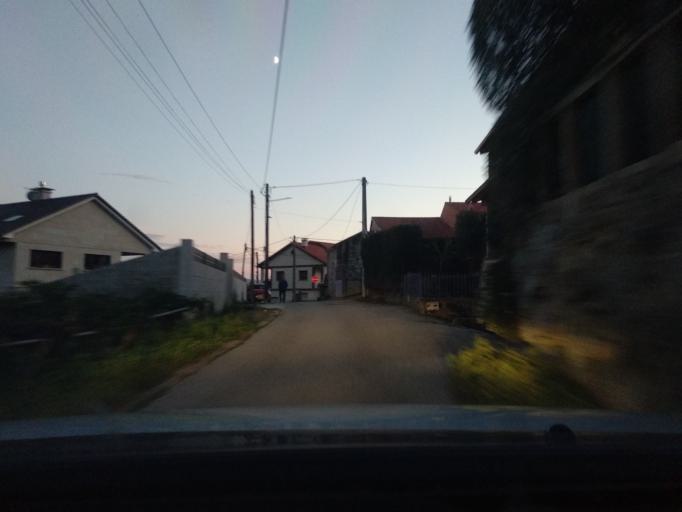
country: ES
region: Galicia
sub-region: Provincia de Pontevedra
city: Moana
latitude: 42.2873
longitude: -8.7510
